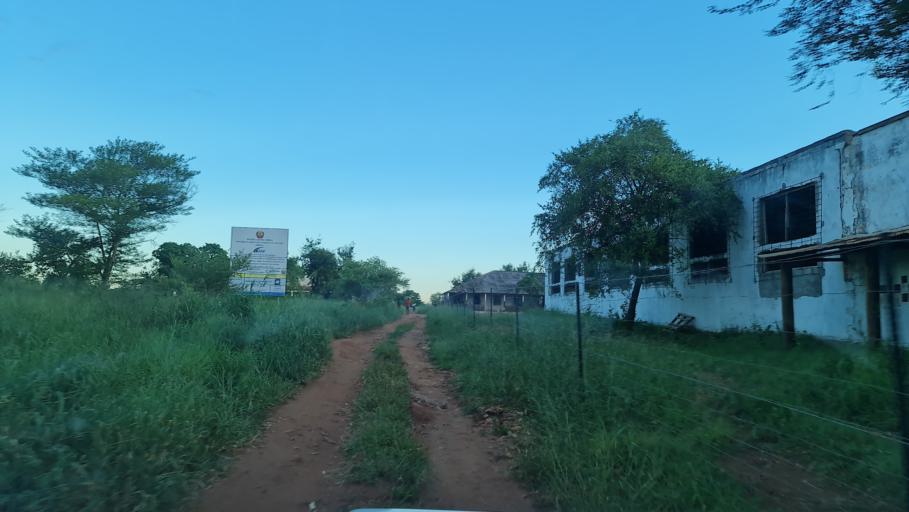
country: MZ
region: Nampula
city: Ilha de Mocambique
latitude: -14.9869
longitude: 40.0951
